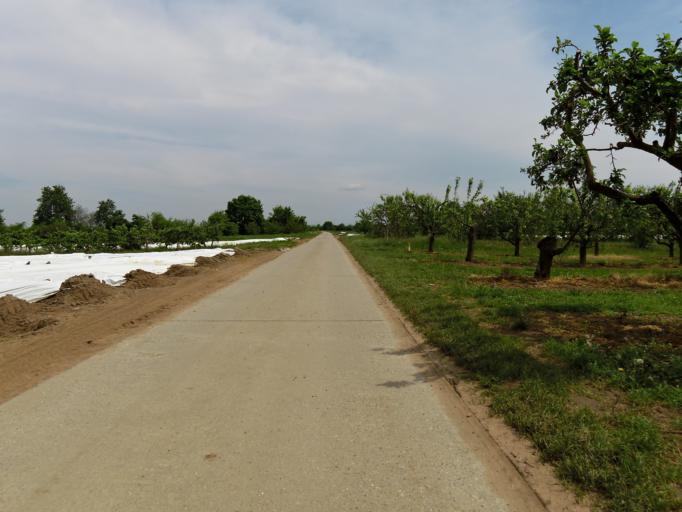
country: DE
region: Rheinland-Pfalz
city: Birkenheide
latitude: 49.4965
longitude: 8.2599
